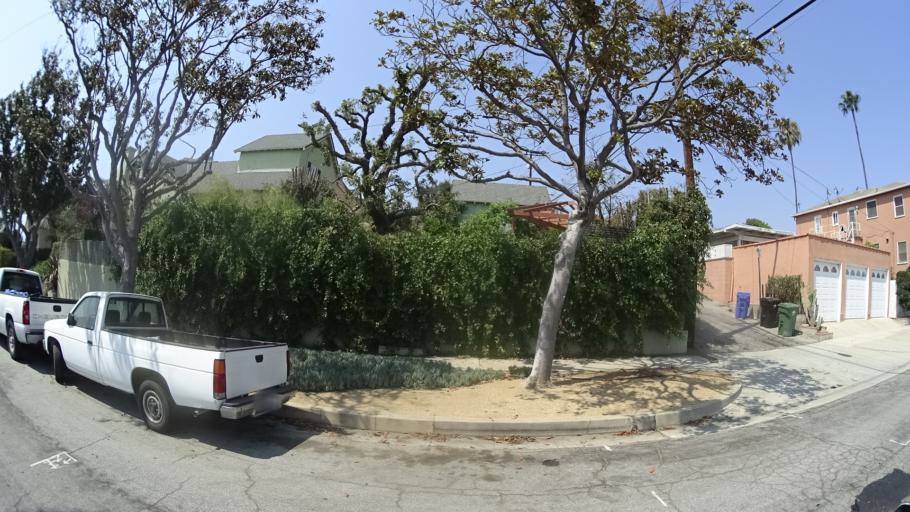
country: US
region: California
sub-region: Los Angeles County
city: View Park-Windsor Hills
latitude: 33.9854
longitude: -118.3554
